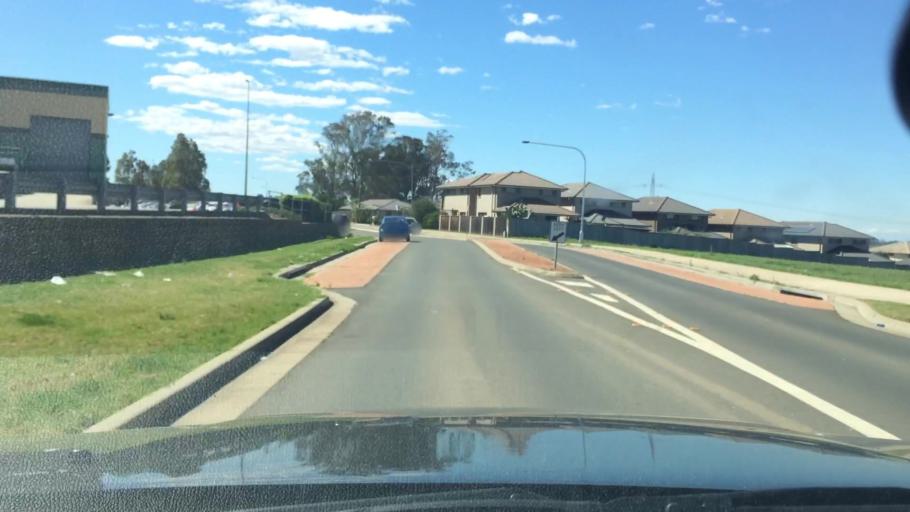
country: AU
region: New South Wales
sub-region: Liverpool
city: Miller
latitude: -33.9384
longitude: 150.8459
